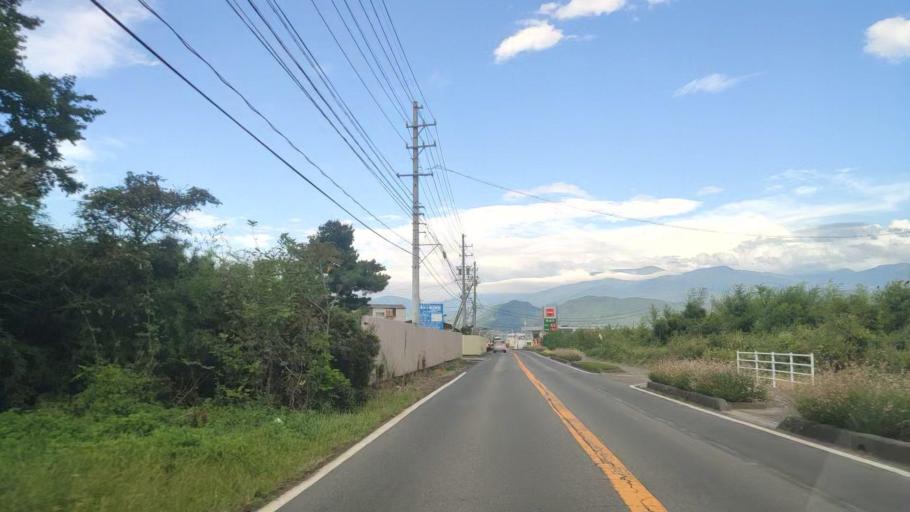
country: JP
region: Nagano
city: Nakano
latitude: 36.7228
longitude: 138.3323
